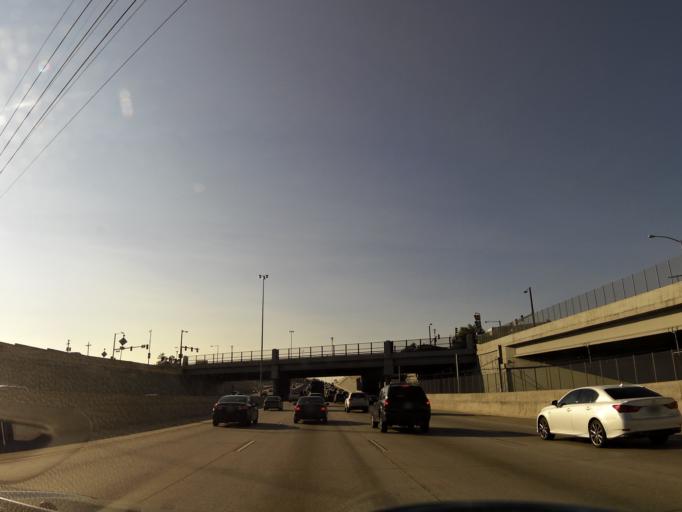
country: US
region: Colorado
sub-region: Arapahoe County
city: Glendale
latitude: 39.6795
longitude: -104.9347
